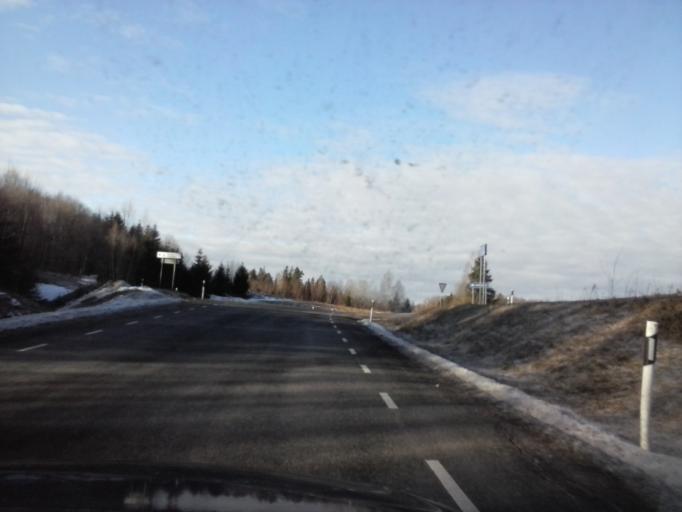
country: EE
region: Tartu
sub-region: Elva linn
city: Elva
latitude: 58.0485
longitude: 26.4237
